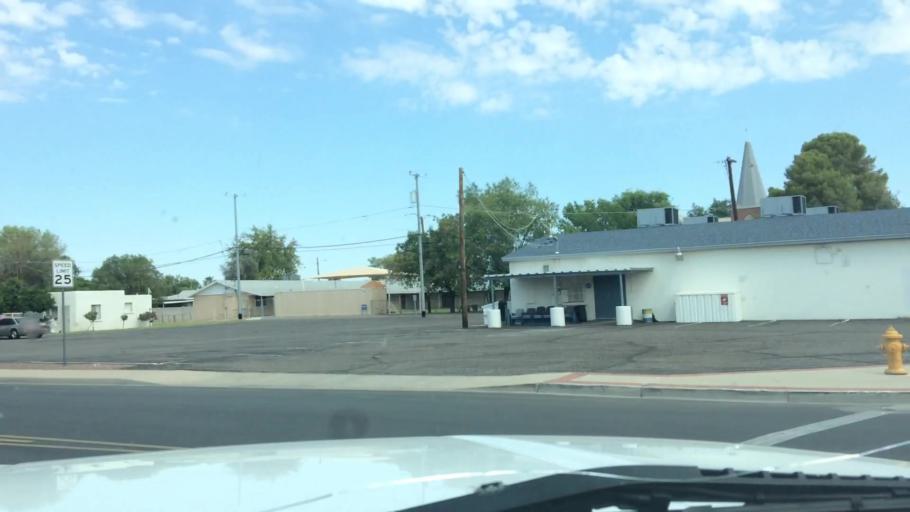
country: US
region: Arizona
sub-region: Maricopa County
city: Peoria
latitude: 33.5774
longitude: -112.2378
